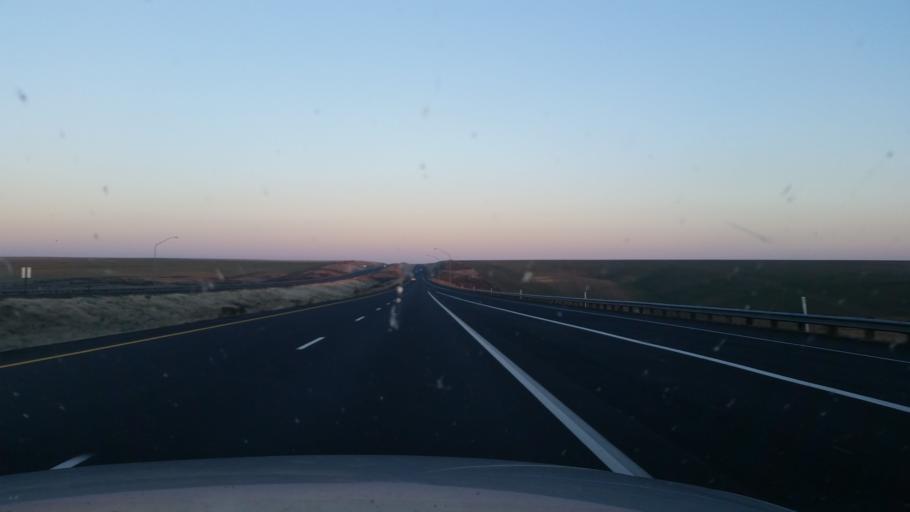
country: US
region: Washington
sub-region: Grant County
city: Warden
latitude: 47.0858
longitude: -118.8378
